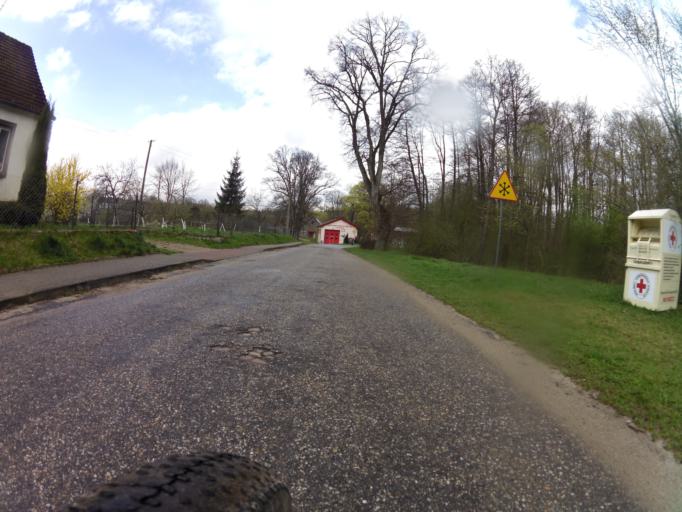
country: PL
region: Pomeranian Voivodeship
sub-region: Powiat slupski
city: Kepice
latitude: 54.2177
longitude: 16.7667
